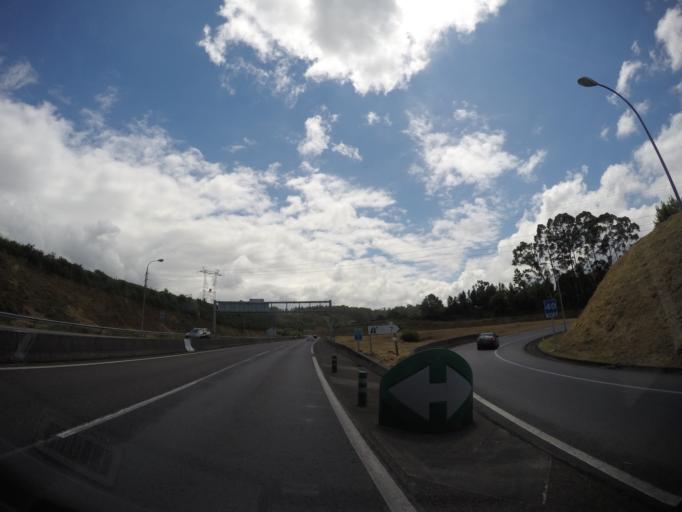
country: ES
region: Galicia
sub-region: Provincia da Coruna
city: Cambre
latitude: 43.3107
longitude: -8.3513
